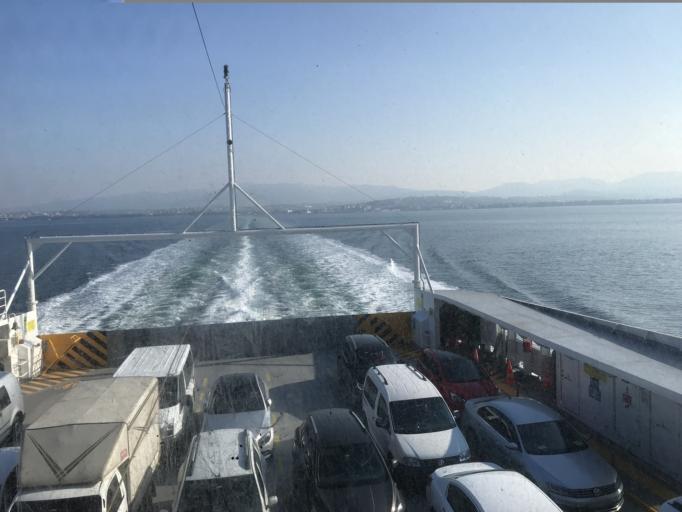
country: TR
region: Yalova
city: Yalova
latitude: 40.6837
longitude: 29.2624
